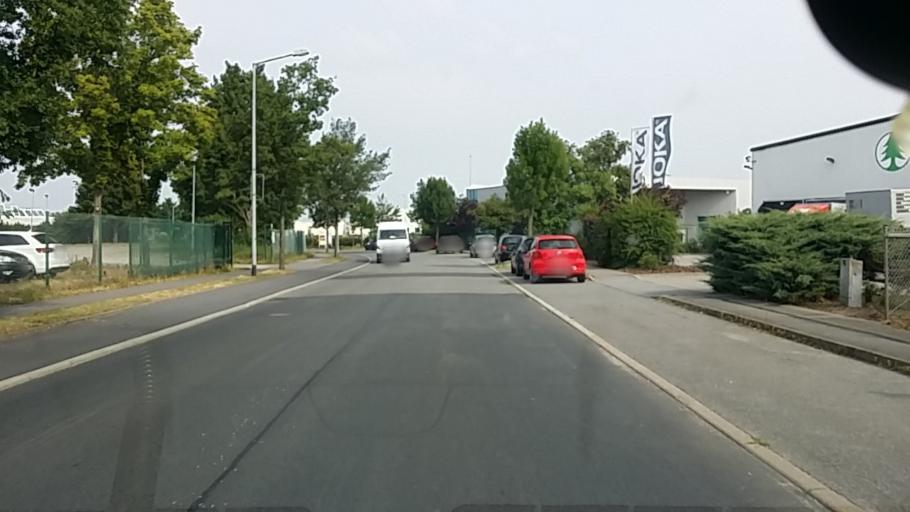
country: DE
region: Saxony
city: Ottendorf-Okrilla
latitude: 51.1757
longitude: 13.8443
